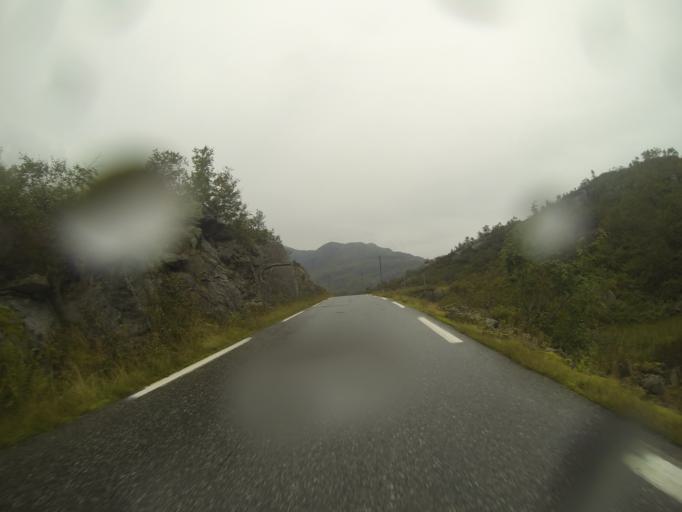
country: NO
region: Rogaland
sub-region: Sauda
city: Sauda
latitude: 59.7257
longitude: 6.5774
